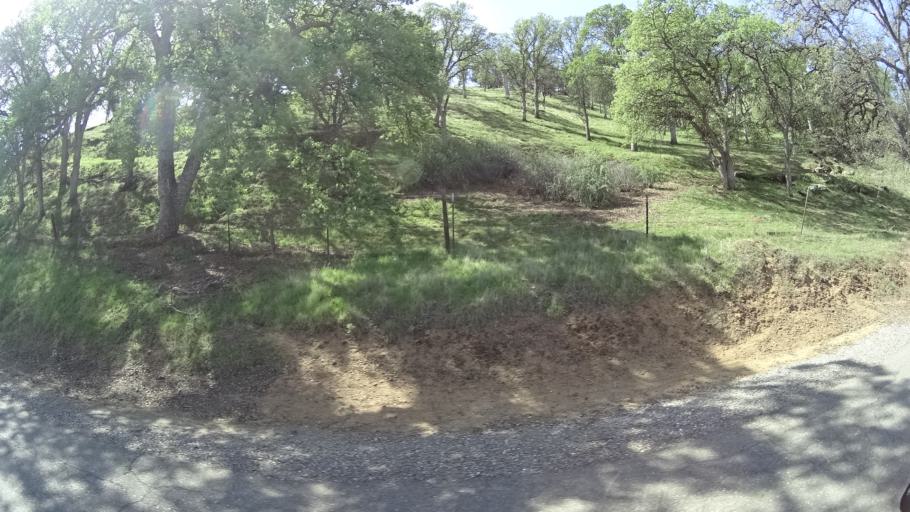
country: US
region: California
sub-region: Glenn County
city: Willows
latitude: 39.5542
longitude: -122.4362
